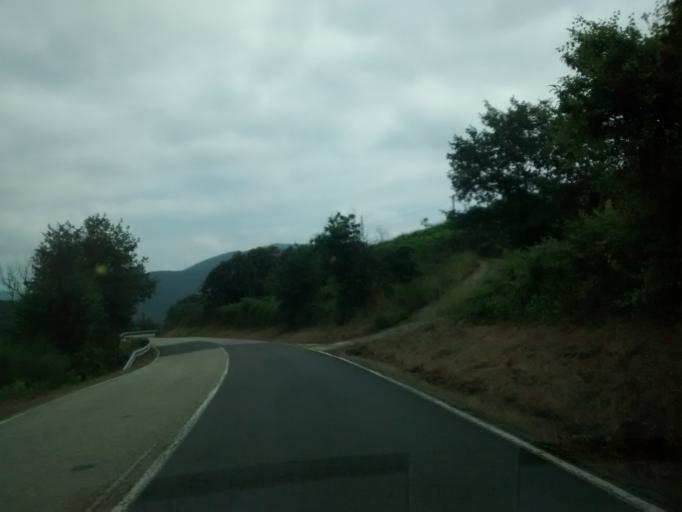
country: ES
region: Galicia
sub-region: Provincia de Ourense
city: Manzaneda
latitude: 42.3387
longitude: -7.2289
